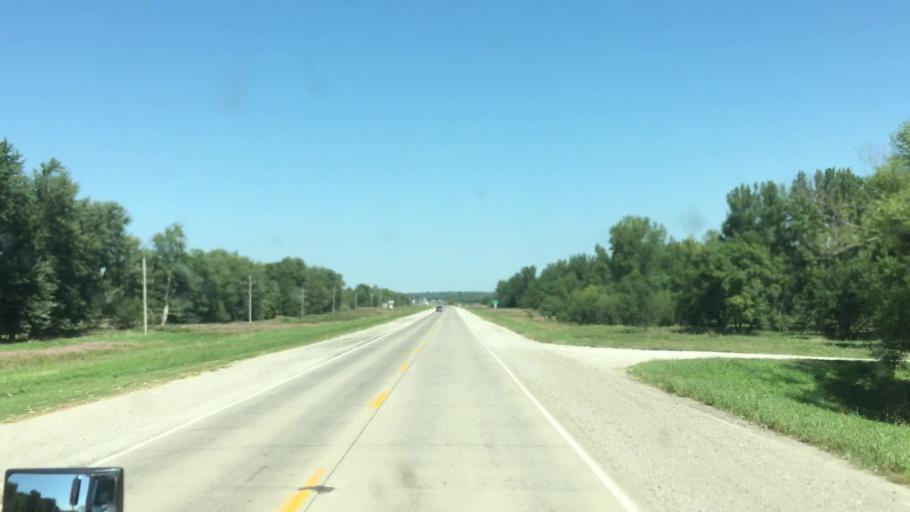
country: US
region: Iowa
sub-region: Benton County
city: Belle Plaine
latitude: 41.8615
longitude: -92.2779
